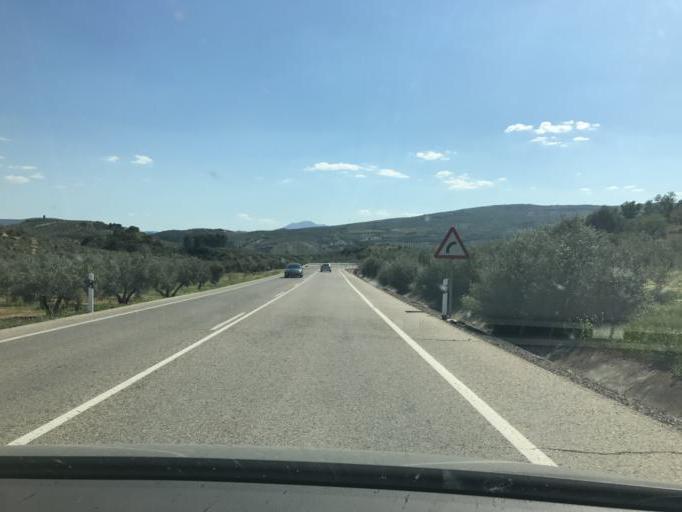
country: ES
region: Andalusia
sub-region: Province of Cordoba
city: Fuente-Tojar
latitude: 37.5689
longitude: -4.1782
